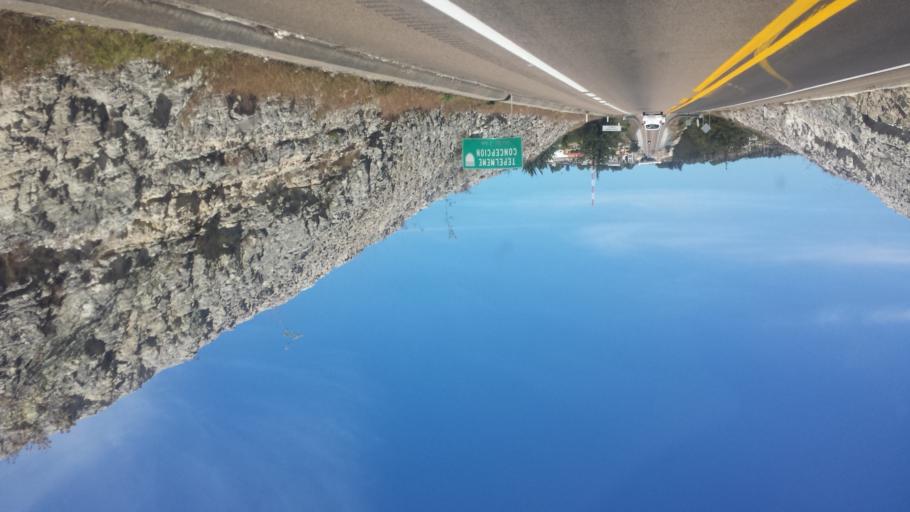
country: MX
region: Oaxaca
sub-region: Villa Tejupam de la Union
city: Villa Tejupam de la Union
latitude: 17.8741
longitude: -97.3752
